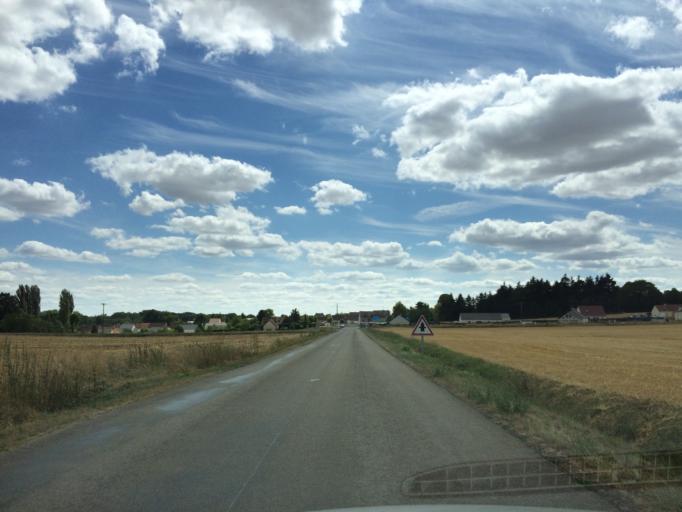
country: FR
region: Bourgogne
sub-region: Departement de l'Yonne
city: Fleury-la-Vallee
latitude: 47.8979
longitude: 3.4287
